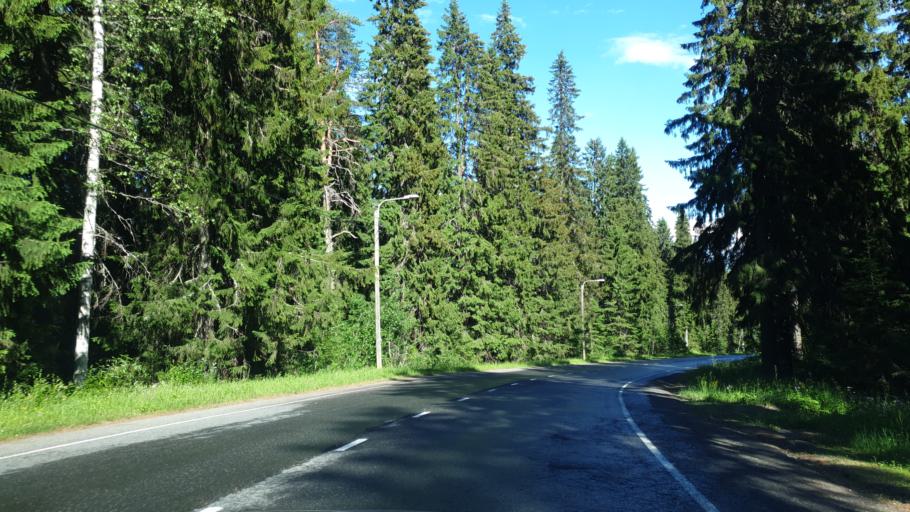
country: FI
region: Northern Savo
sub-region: Kuopio
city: Kuopio
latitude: 62.9090
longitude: 27.6601
